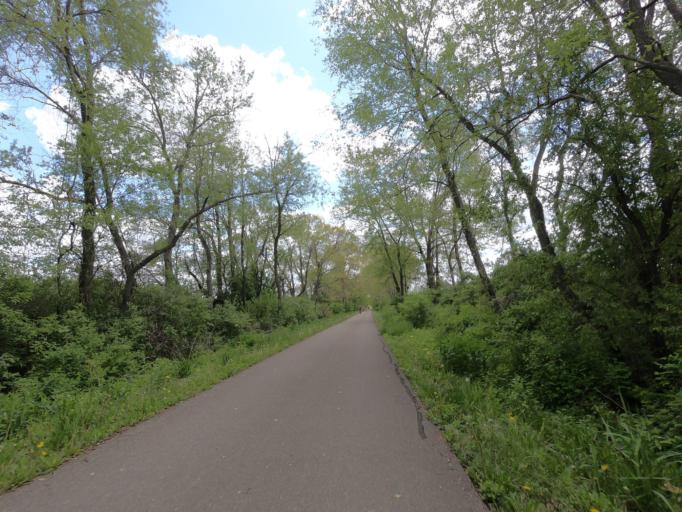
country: US
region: Wisconsin
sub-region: Dane County
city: Fitchburg
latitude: 42.9713
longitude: -89.4647
